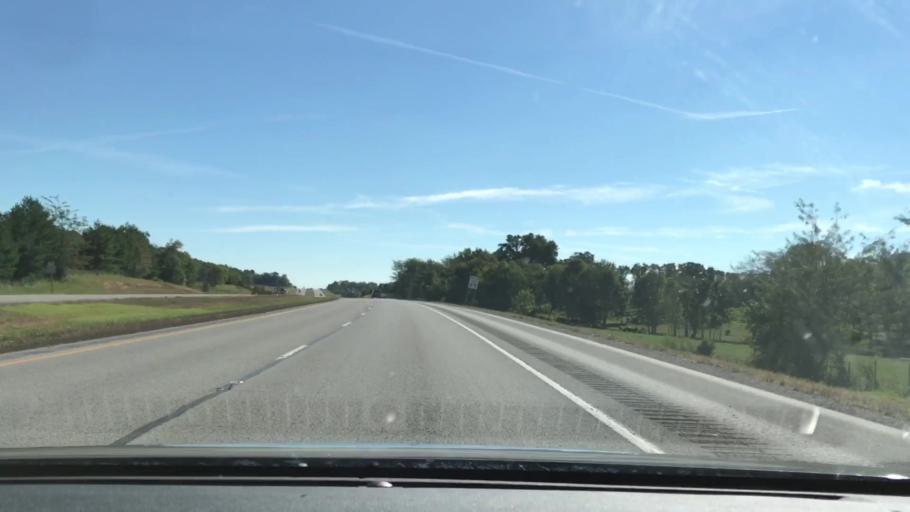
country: US
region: Kentucky
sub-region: Todd County
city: Elkton
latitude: 36.8265
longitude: -87.2193
